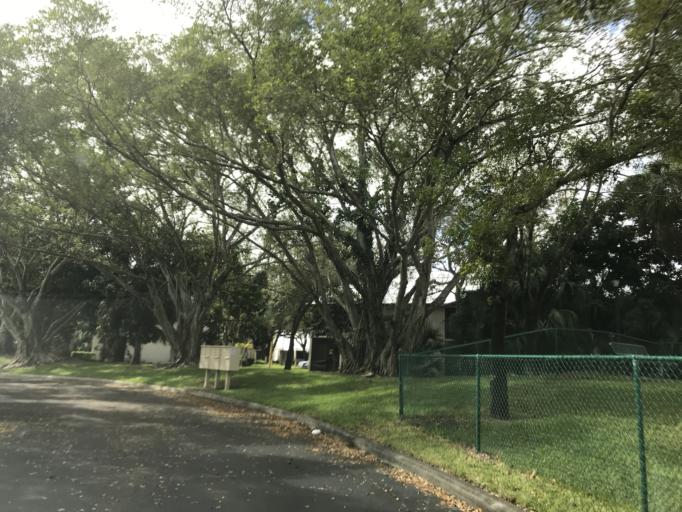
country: US
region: Florida
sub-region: Broward County
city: Coconut Creek
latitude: 26.2735
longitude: -80.1882
